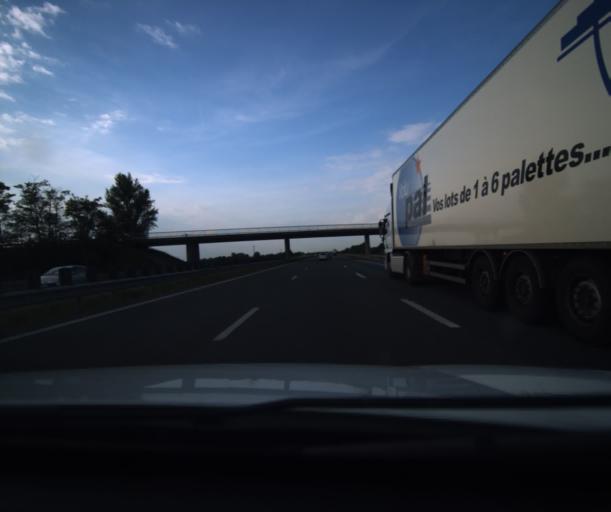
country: FR
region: Midi-Pyrenees
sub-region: Departement du Tarn-et-Garonne
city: Grisolles
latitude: 43.8588
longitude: 1.3184
